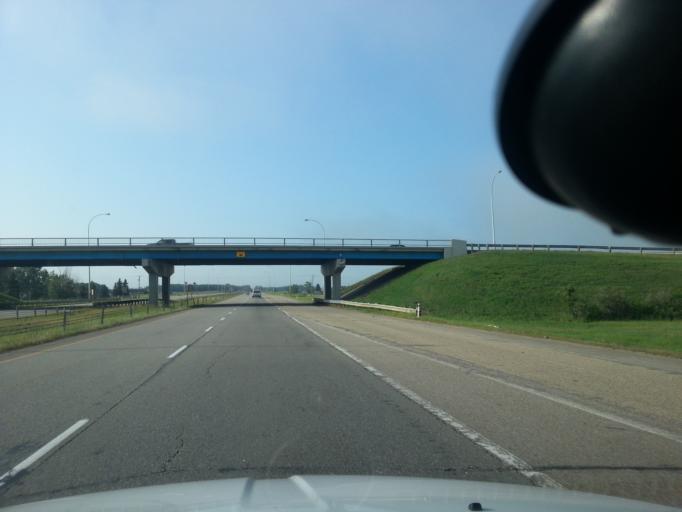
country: CA
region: Alberta
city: Leduc
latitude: 53.2534
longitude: -113.5619
